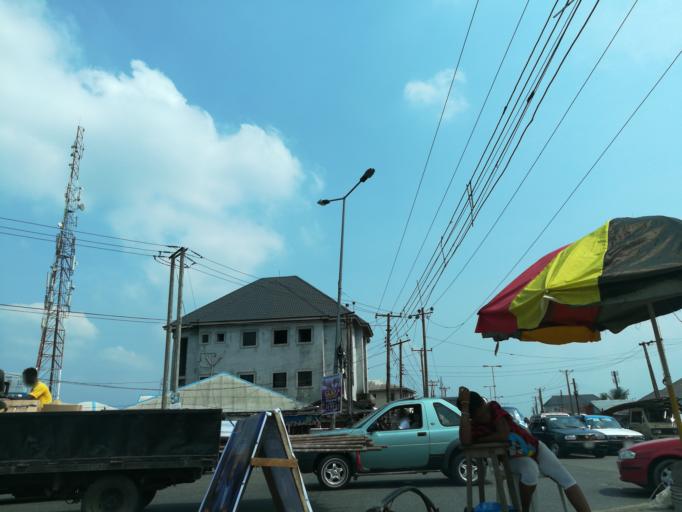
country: NG
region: Rivers
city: Port Harcourt
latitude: 4.8305
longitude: 6.9819
